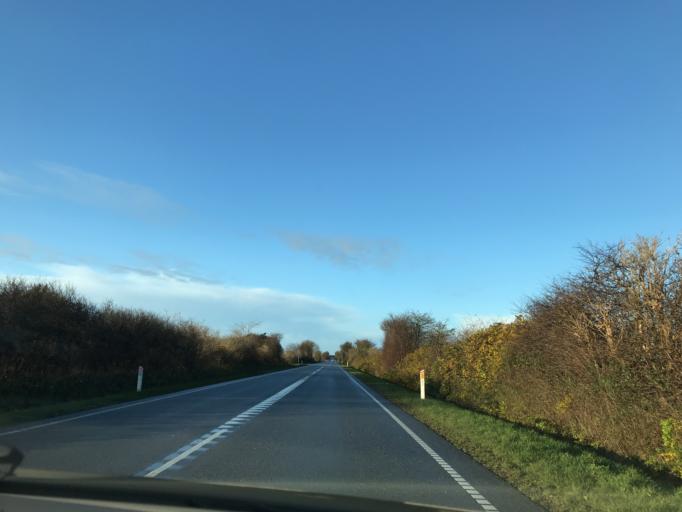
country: DK
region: South Denmark
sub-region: Haderslev Kommune
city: Vojens
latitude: 55.1728
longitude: 9.3290
